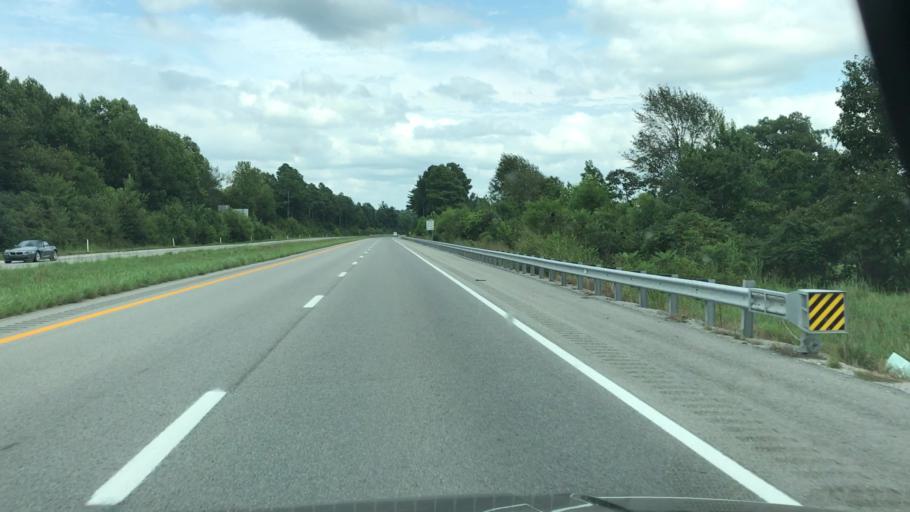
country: US
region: Kentucky
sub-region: Hopkins County
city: Dawson Springs
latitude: 37.1994
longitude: -87.6756
